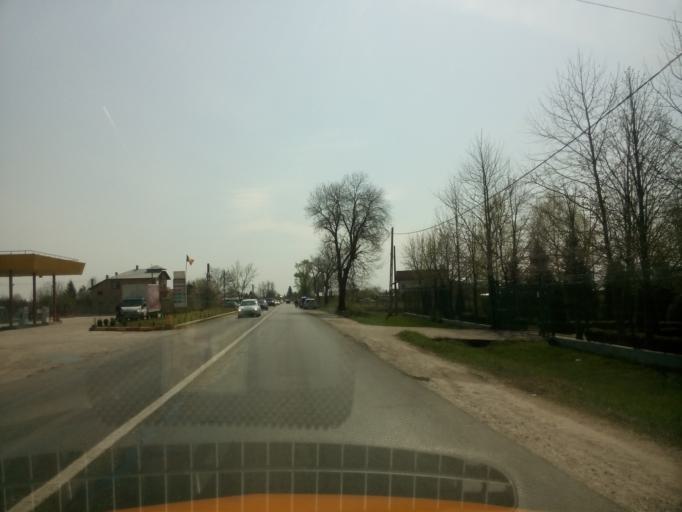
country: RO
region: Calarasi
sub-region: Comuna Frumusani
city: Frumusani
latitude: 44.3047
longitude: 26.3004
